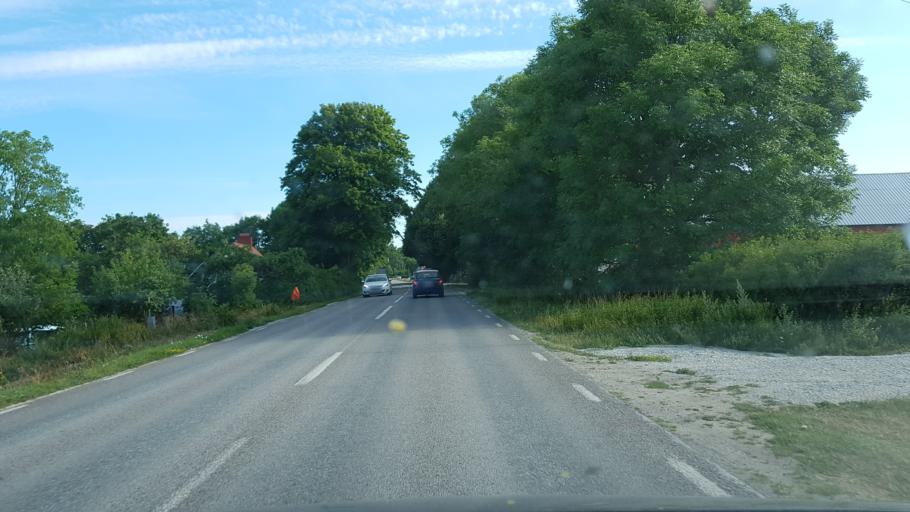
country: SE
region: Gotland
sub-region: Gotland
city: Visby
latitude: 57.7557
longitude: 18.4253
